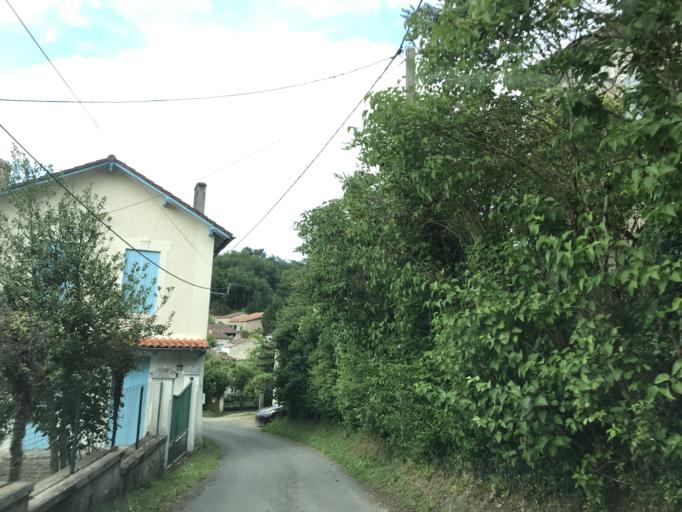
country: FR
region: Poitou-Charentes
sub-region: Departement de la Charente
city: Chalais
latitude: 45.2331
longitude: 0.0379
